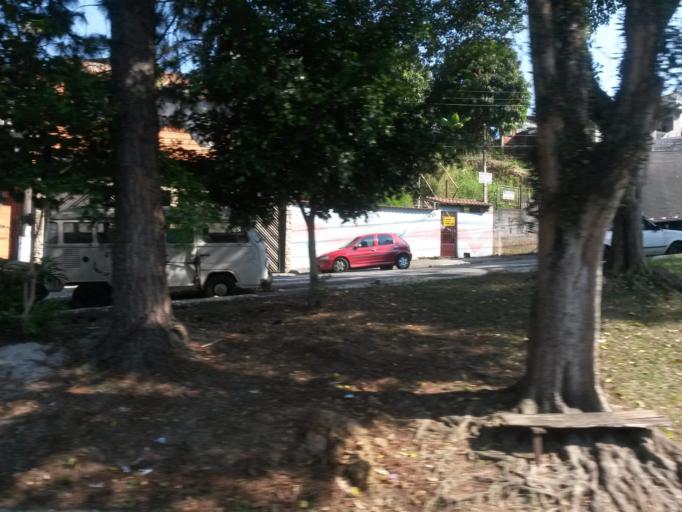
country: BR
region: Sao Paulo
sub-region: Sao Bernardo Do Campo
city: Sao Bernardo do Campo
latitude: -23.7016
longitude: -46.5691
